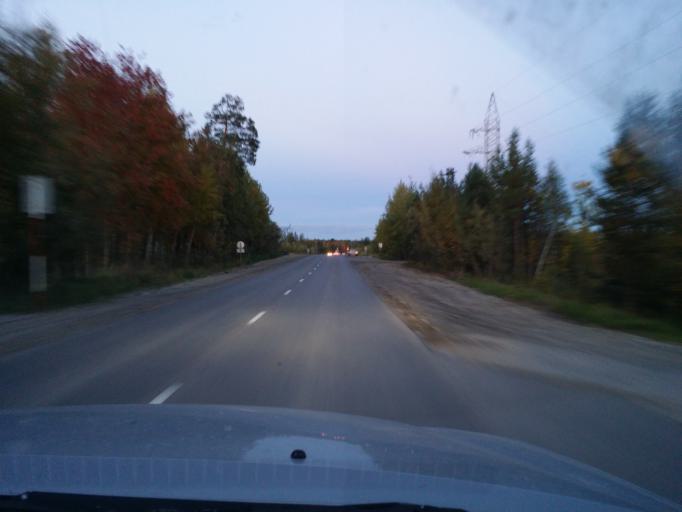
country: RU
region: Khanty-Mansiyskiy Avtonomnyy Okrug
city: Nizhnevartovsk
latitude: 60.9920
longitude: 76.4272
